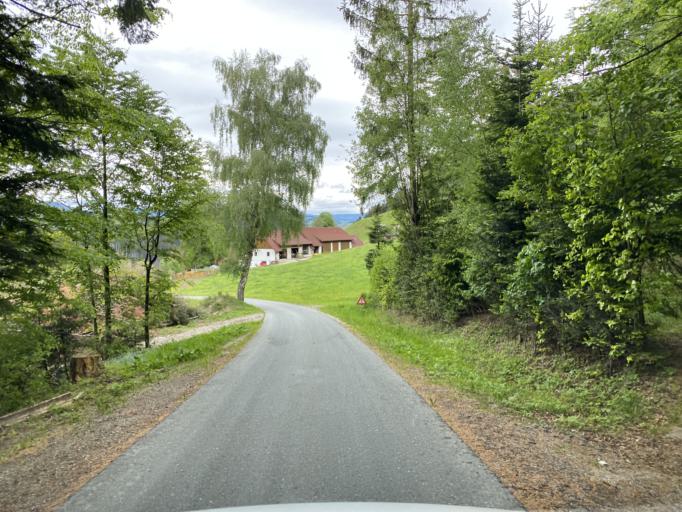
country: AT
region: Styria
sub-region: Politischer Bezirk Weiz
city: Koglhof
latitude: 47.3262
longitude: 15.7007
